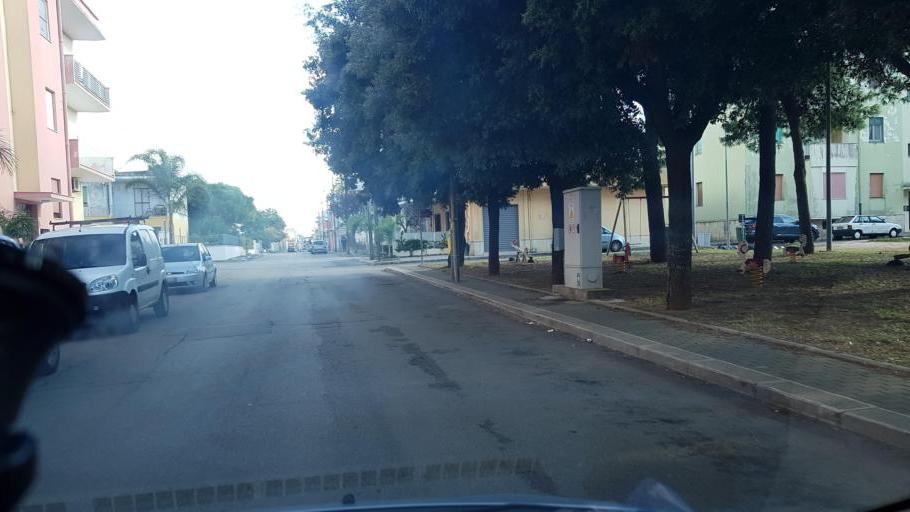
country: IT
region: Apulia
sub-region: Provincia di Lecce
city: Squinzano
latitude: 40.4378
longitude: 18.0343
